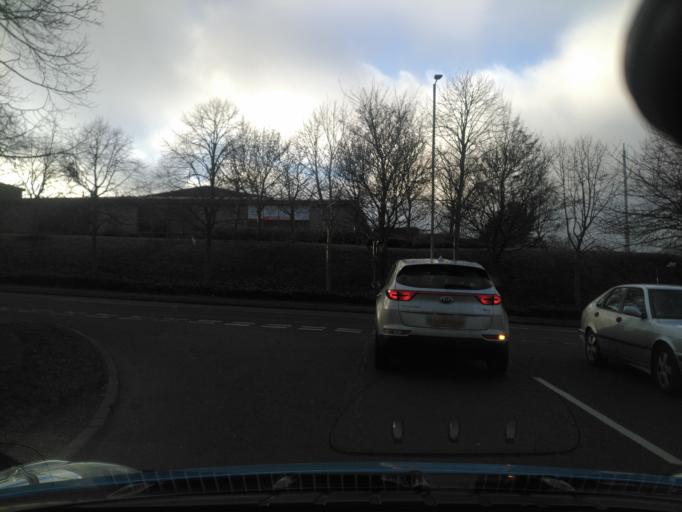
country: GB
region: England
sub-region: Hertfordshire
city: Letchworth Garden City
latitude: 51.9804
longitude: -0.2072
